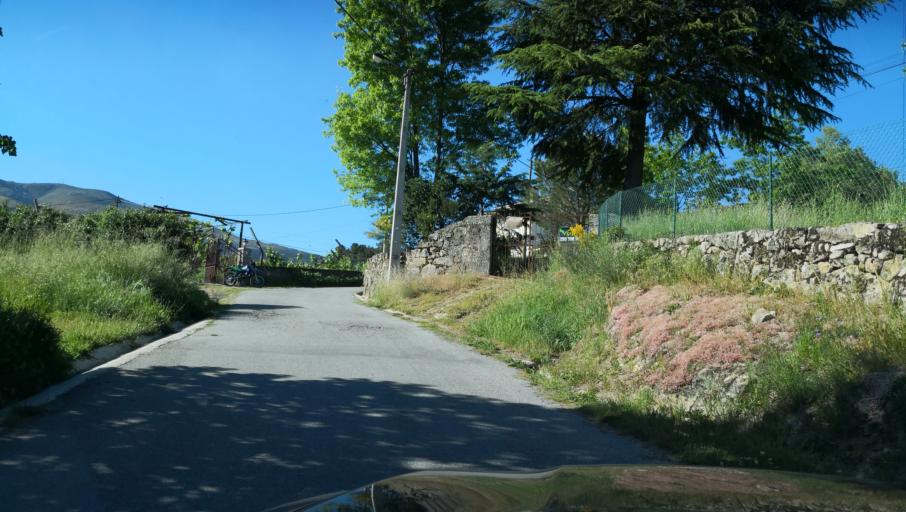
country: PT
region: Vila Real
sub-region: Vila Real
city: Vila Real
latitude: 41.3265
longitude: -7.7357
